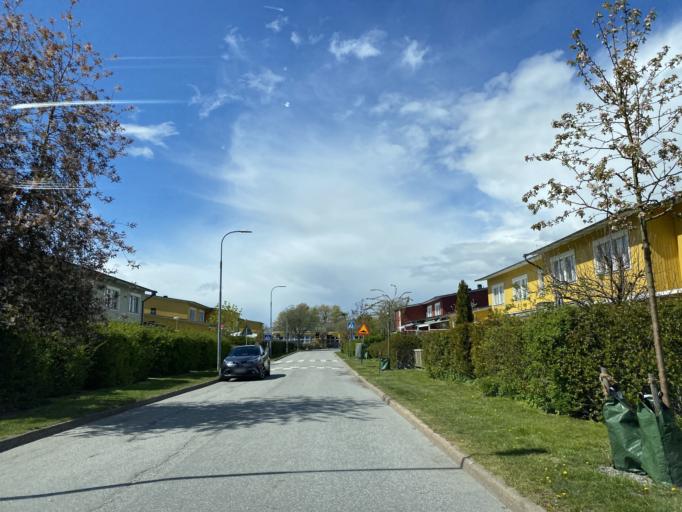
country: SE
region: Stockholm
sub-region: Stockholms Kommun
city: Kista
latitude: 59.4099
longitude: 17.9173
